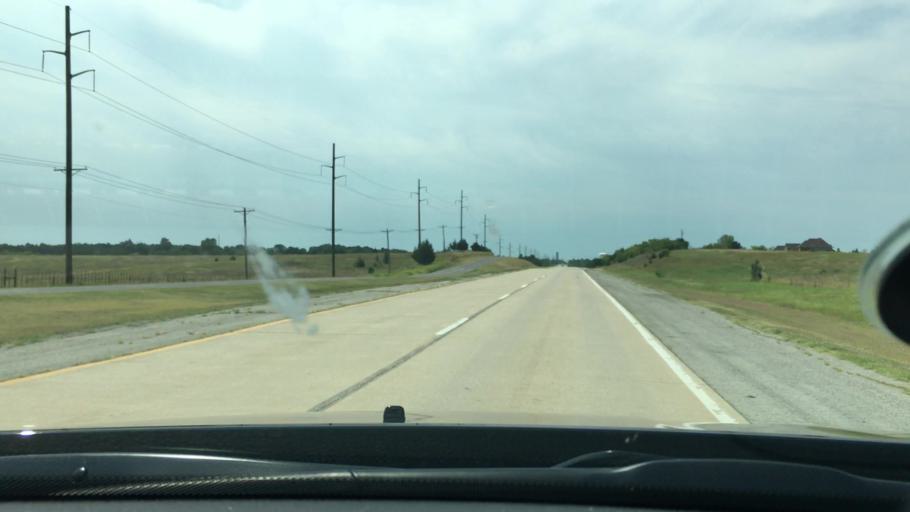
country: US
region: Oklahoma
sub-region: Carter County
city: Ardmore
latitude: 34.2298
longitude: -97.1433
